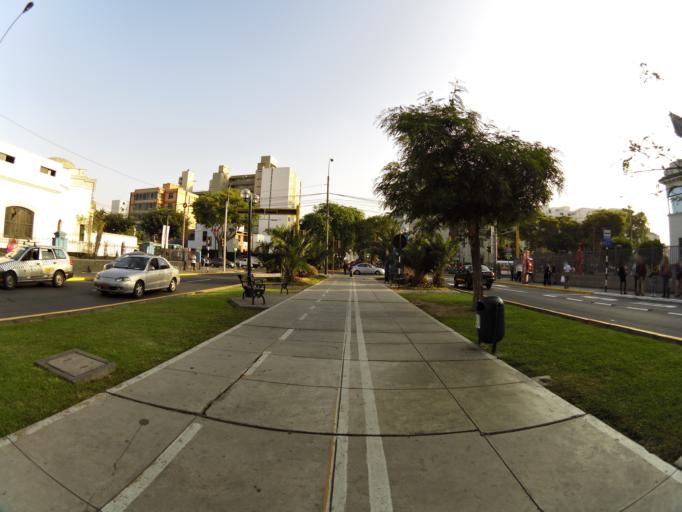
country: PE
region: Lima
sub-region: Lima
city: San Isidro
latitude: -12.1133
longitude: -77.0300
